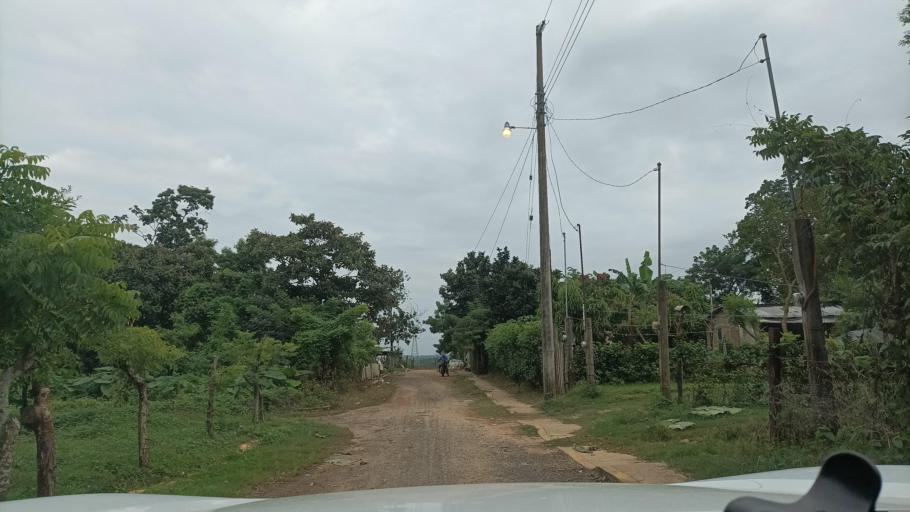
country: MX
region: Veracruz
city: Oteapan
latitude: 17.9880
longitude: -94.6732
